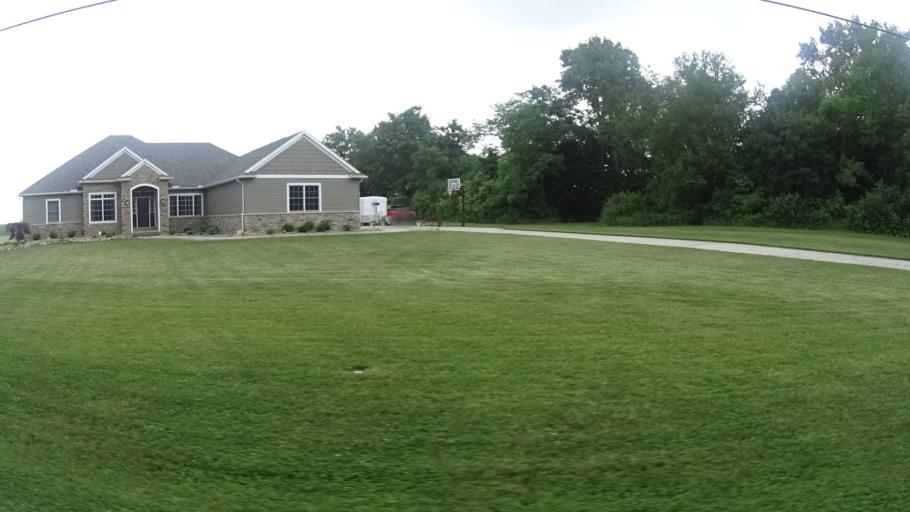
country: US
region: Ohio
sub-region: Huron County
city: Monroeville
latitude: 41.3429
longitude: -82.7411
